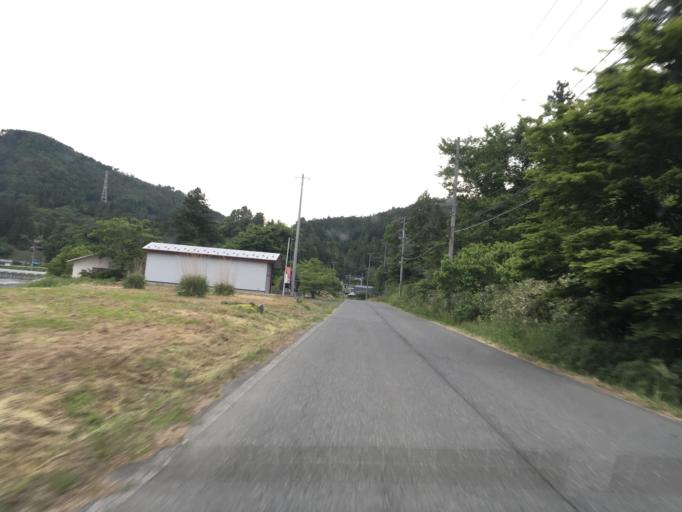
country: JP
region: Iwate
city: Mizusawa
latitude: 39.1775
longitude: 141.2922
